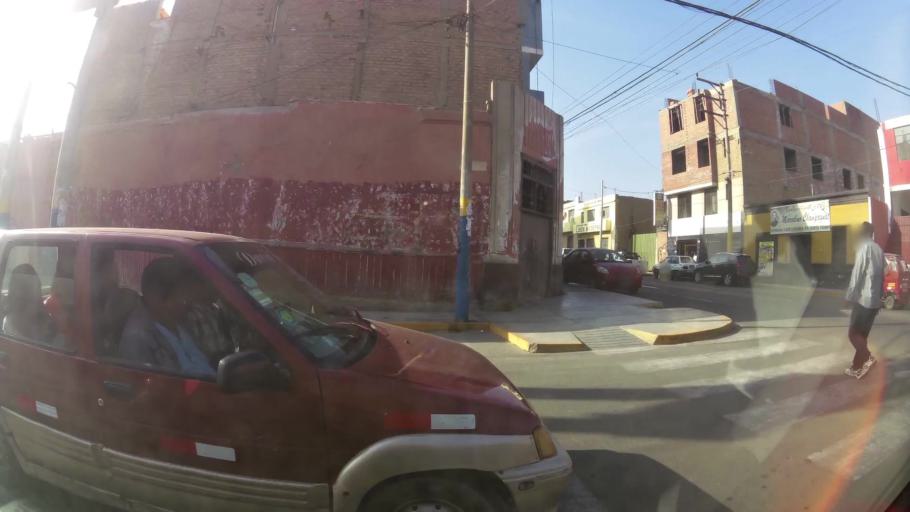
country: PE
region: Lima
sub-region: Huaura
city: Huacho
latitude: -11.1108
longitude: -77.6102
